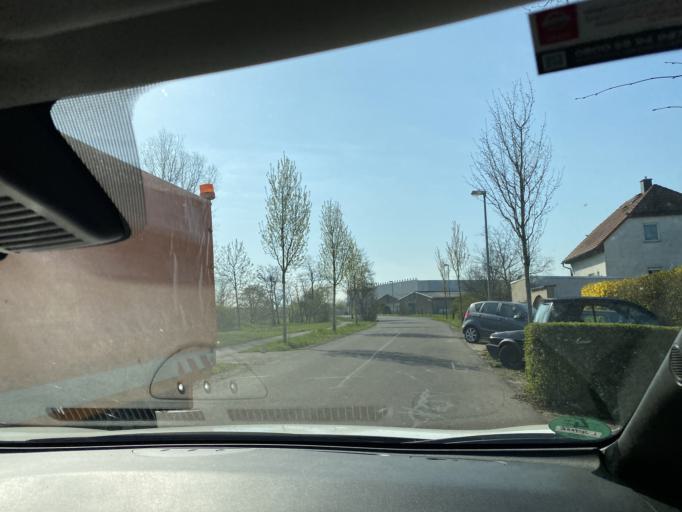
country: DE
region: Saxony
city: Kitzen
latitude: 51.2519
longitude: 12.2724
